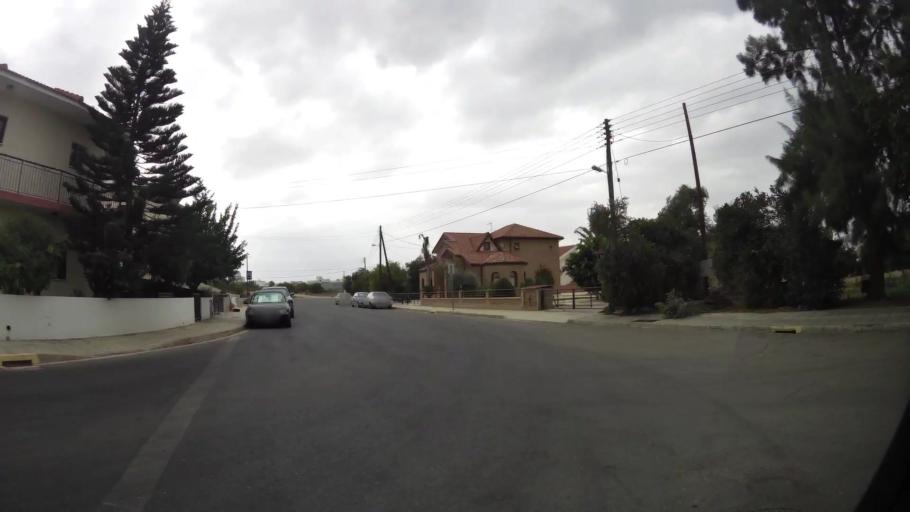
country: CY
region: Lefkosia
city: Geri
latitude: 35.1081
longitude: 33.3891
